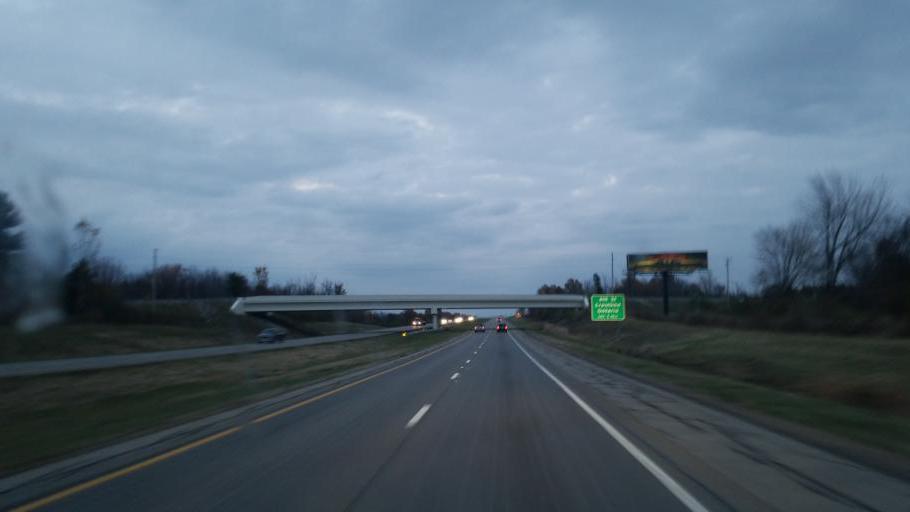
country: US
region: Ohio
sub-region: Crawford County
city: Crestline
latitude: 40.7671
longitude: -82.6821
